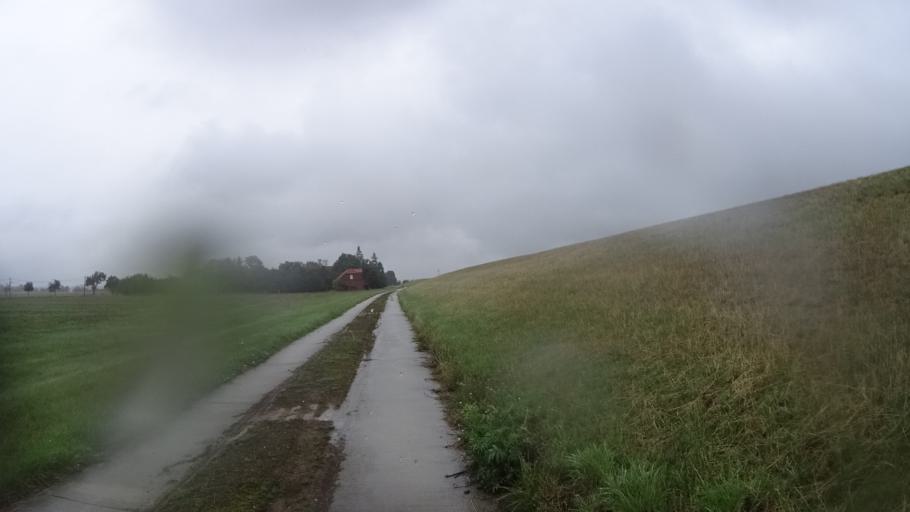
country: DE
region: Lower Saxony
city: Dannenberg
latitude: 53.1554
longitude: 11.1107
